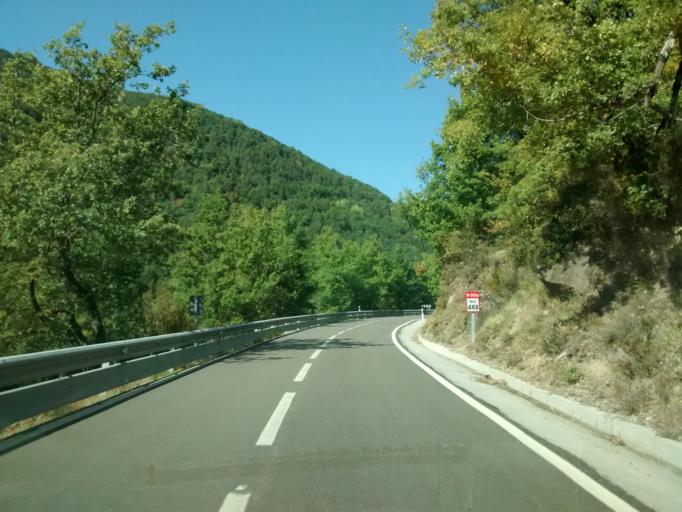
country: ES
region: Aragon
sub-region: Provincia de Huesca
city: Fiscal
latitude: 42.5309
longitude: -0.1382
